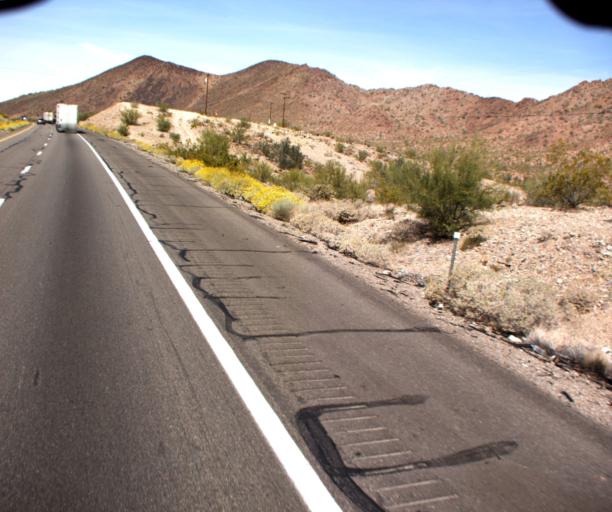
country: US
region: Arizona
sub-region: La Paz County
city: Quartzsite
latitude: 33.6742
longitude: -114.0496
